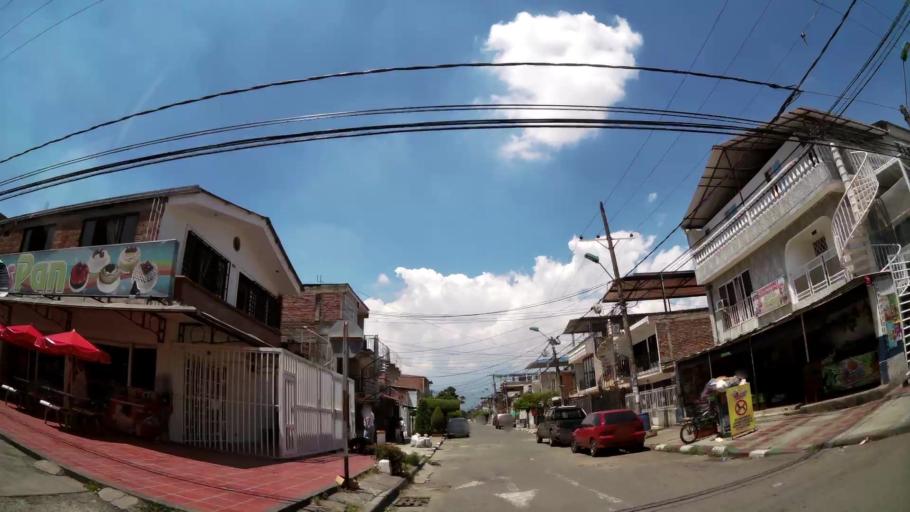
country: CO
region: Valle del Cauca
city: Cali
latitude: 3.4399
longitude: -76.4952
